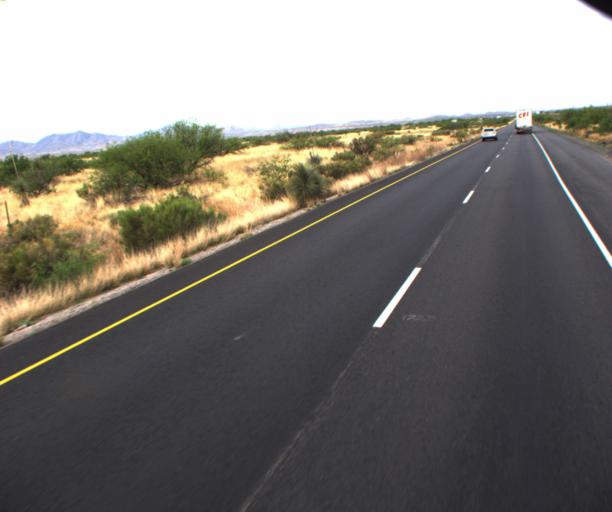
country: US
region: Arizona
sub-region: Cochise County
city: Mescal
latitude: 31.9743
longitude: -110.4973
